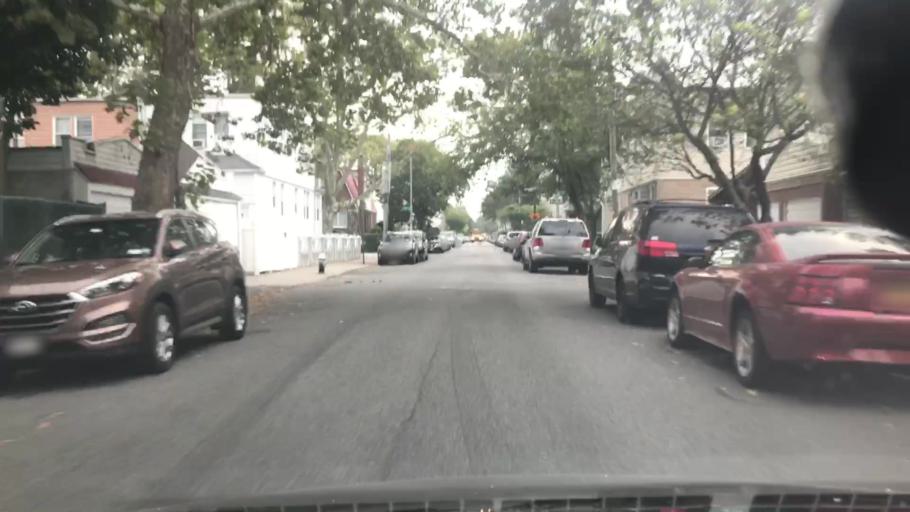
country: US
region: New York
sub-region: Kings County
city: East New York
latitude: 40.7044
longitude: -73.8887
